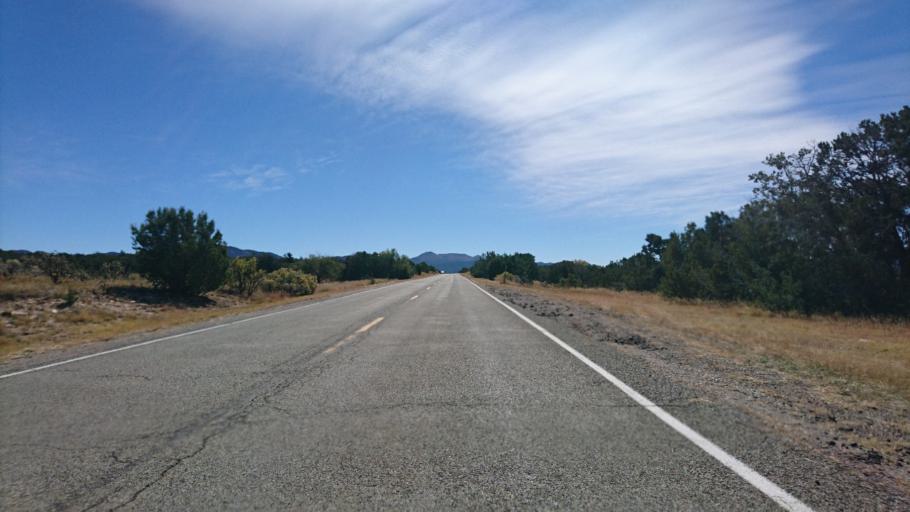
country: US
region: New Mexico
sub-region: Bernalillo County
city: Sandia Knolls
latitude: 35.3083
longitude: -106.2154
